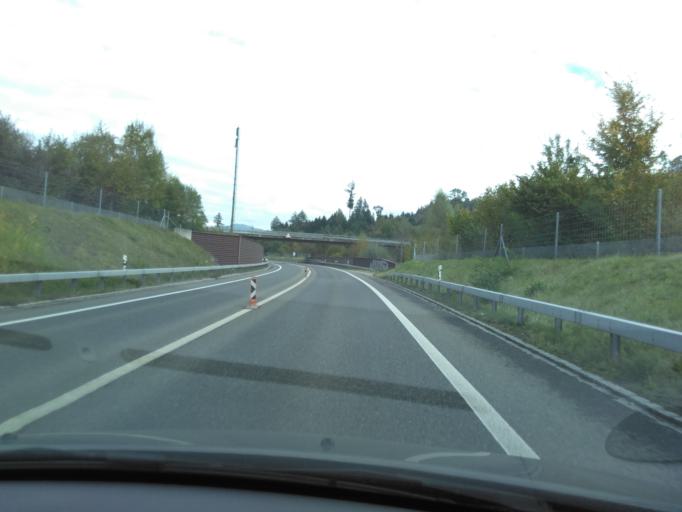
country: CH
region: Saint Gallen
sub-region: Wahlkreis See-Gaster
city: Eschenbach
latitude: 47.2283
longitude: 8.8903
